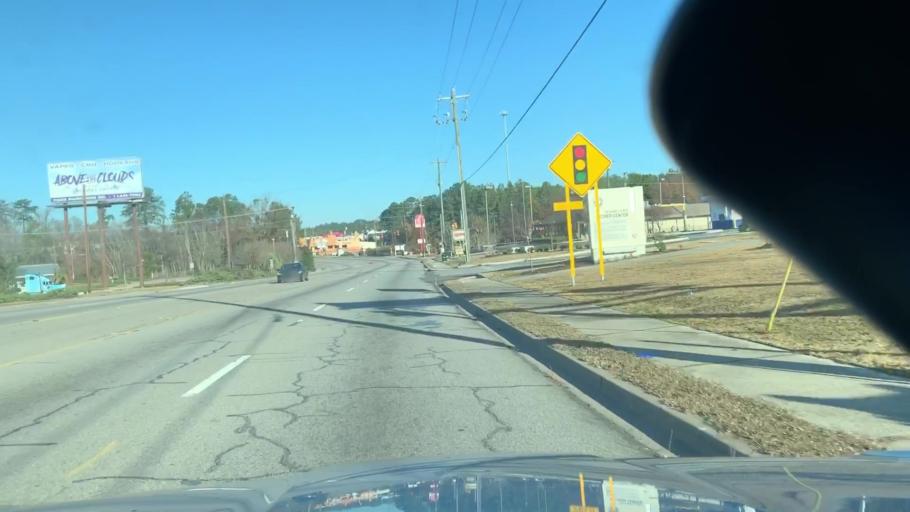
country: US
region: South Carolina
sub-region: Richland County
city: Dentsville
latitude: 34.0585
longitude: -80.9505
